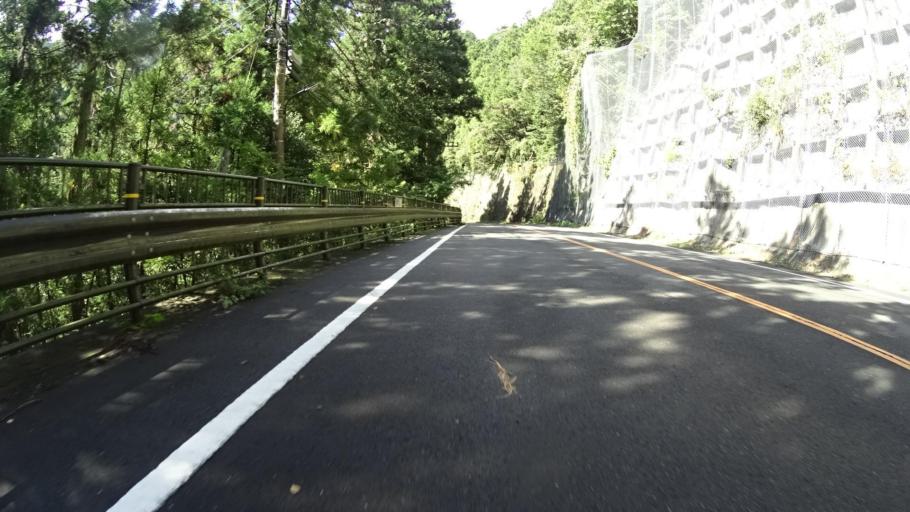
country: JP
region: Yamanashi
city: Uenohara
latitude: 35.7394
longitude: 139.0880
